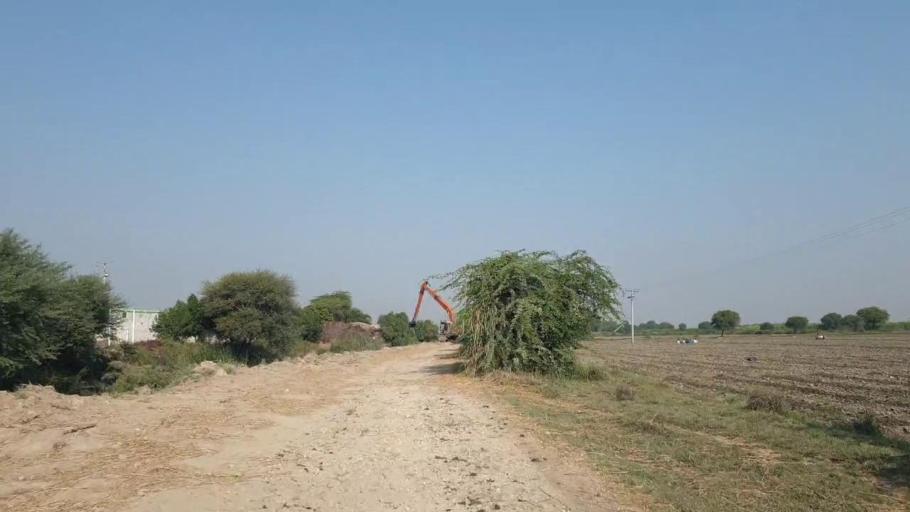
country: PK
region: Sindh
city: Matli
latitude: 24.9915
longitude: 68.6222
